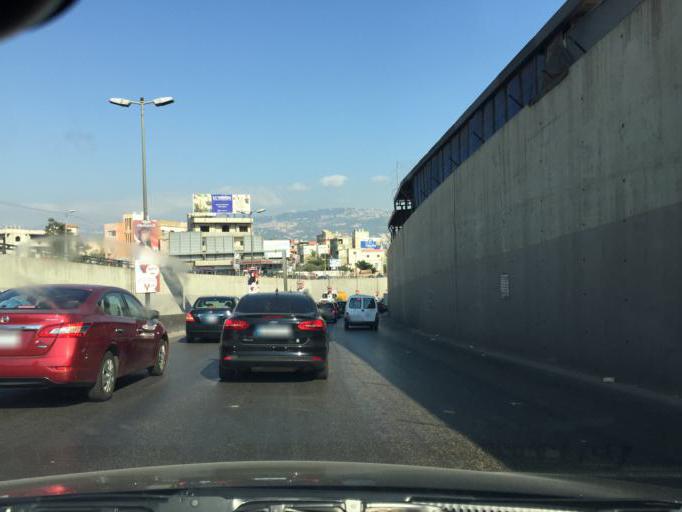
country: LB
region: Mont-Liban
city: Baabda
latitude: 33.8328
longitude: 35.4993
